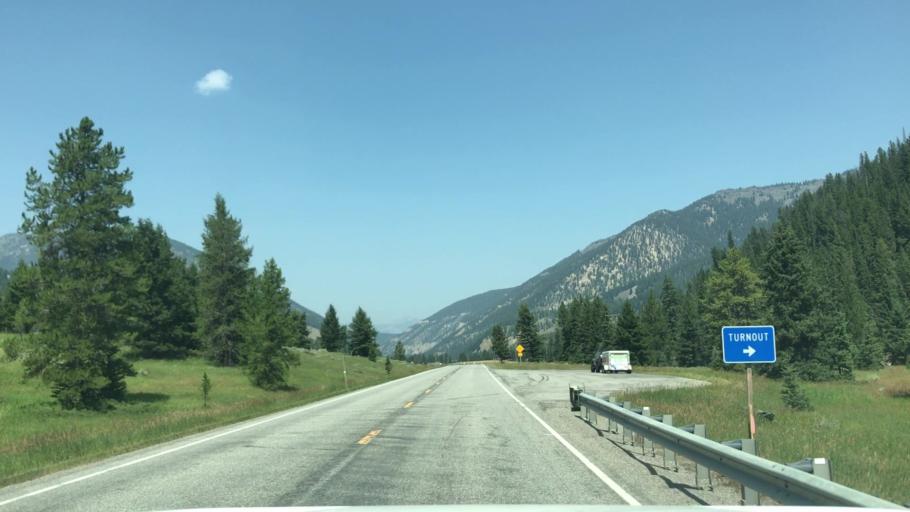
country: US
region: Montana
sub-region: Gallatin County
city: Big Sky
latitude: 45.0901
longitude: -111.2134
